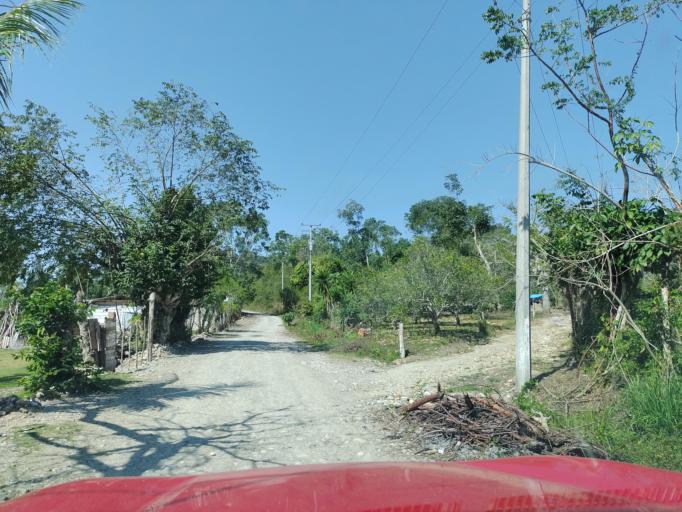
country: MX
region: Veracruz
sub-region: Papantla
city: Polutla
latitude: 20.5015
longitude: -97.2163
